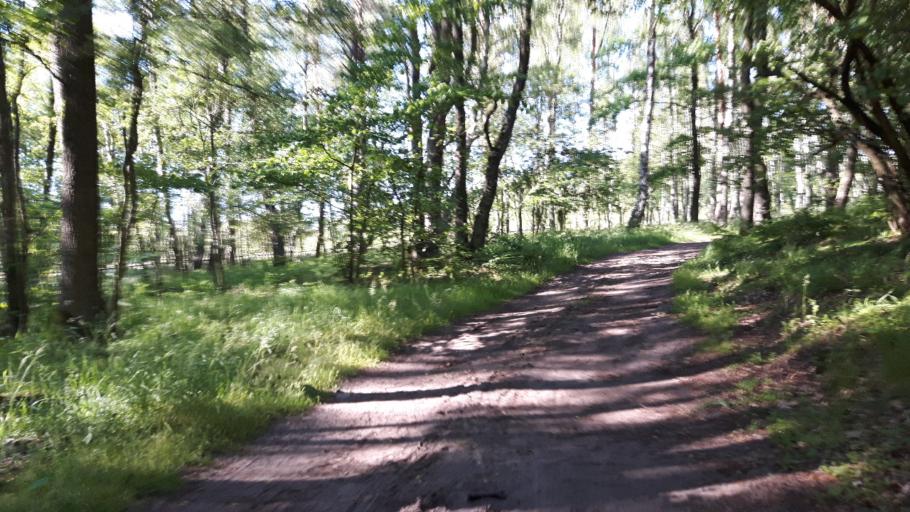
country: PL
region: Pomeranian Voivodeship
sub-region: Powiat leborski
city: Leba
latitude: 54.7149
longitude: 17.5255
